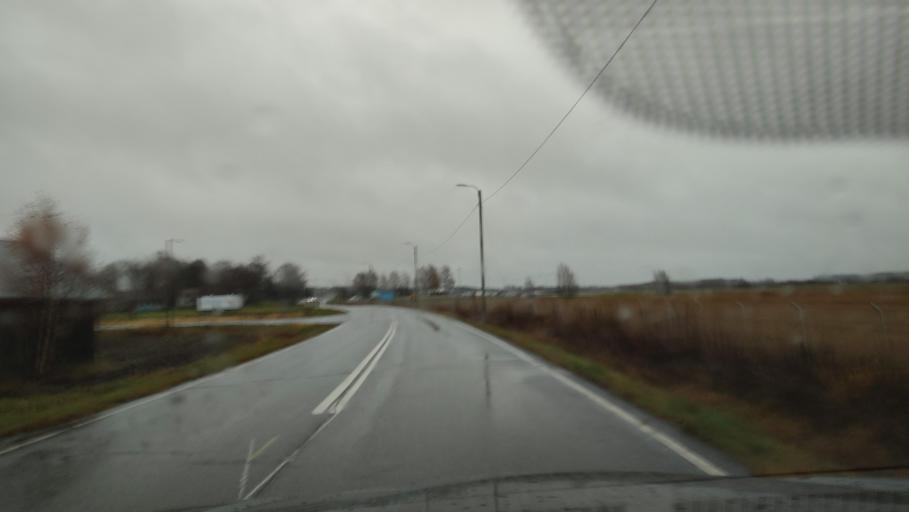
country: FI
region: Ostrobothnia
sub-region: Vaasa
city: Ristinummi
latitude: 63.0439
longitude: 21.7518
